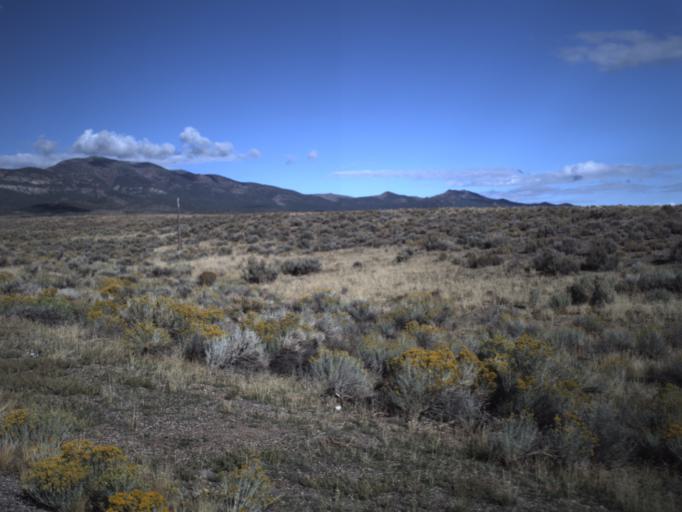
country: US
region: Utah
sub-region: Beaver County
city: Milford
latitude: 38.4479
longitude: -113.1897
